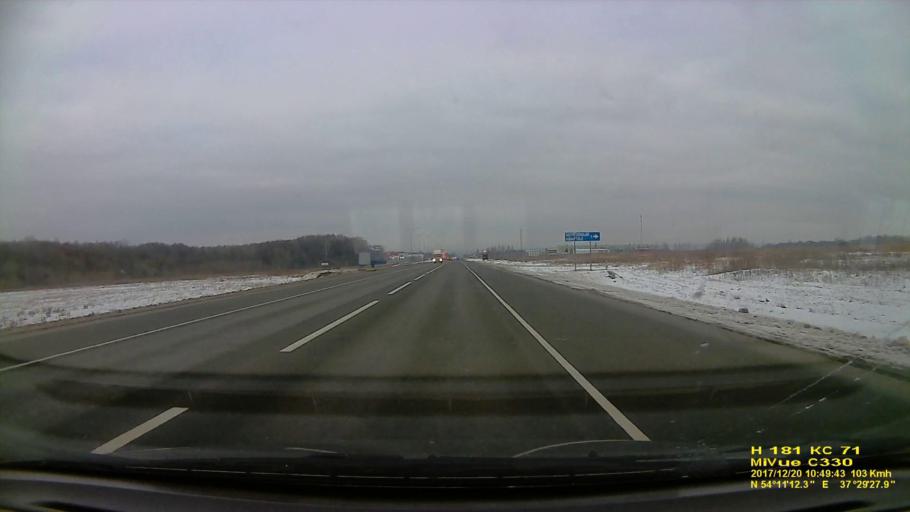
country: RU
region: Tula
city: Barsuki
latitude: 54.1872
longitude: 37.4910
